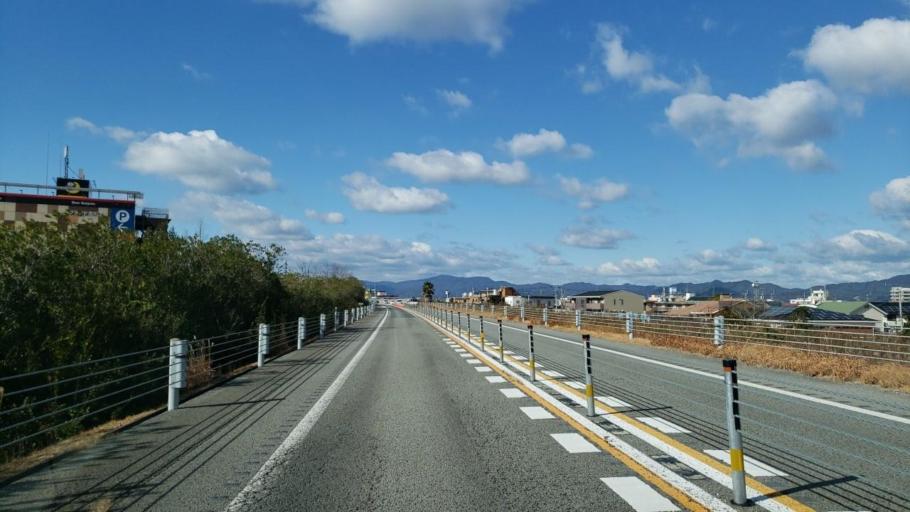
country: JP
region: Tokushima
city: Tokushima-shi
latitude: 34.1036
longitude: 134.5590
